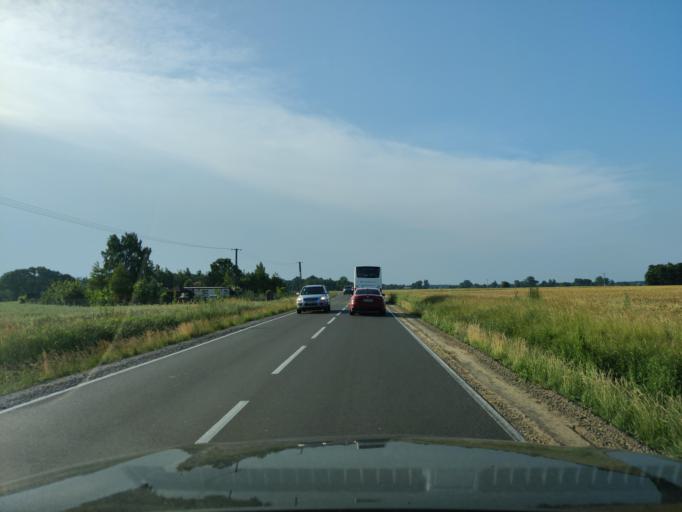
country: PL
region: Masovian Voivodeship
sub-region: Powiat plonski
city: Baboszewo
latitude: 52.7089
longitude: 20.3380
